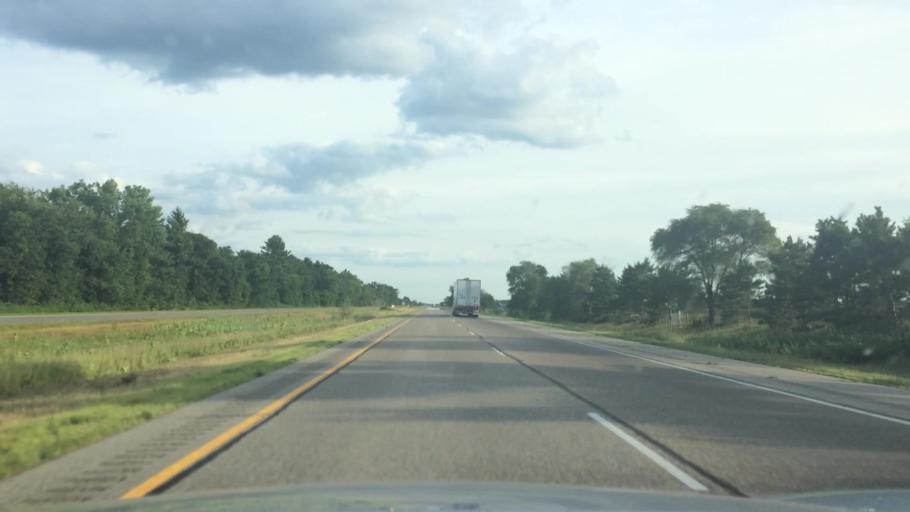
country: US
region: Wisconsin
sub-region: Portage County
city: Plover
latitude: 44.2514
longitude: -89.5242
